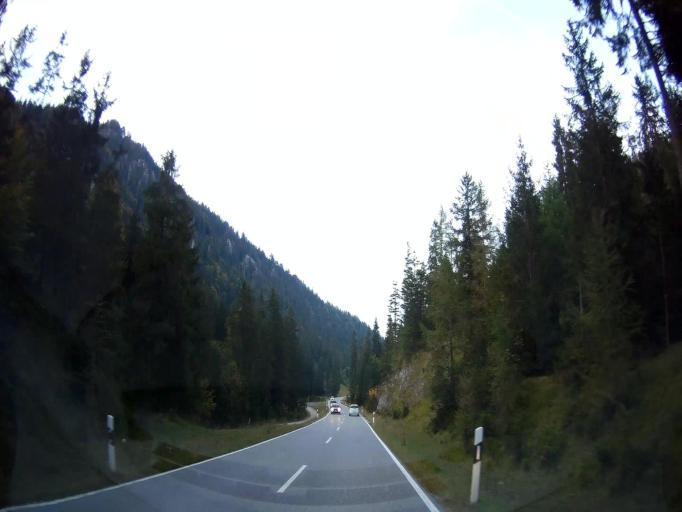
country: DE
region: Bavaria
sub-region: Upper Bavaria
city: Ramsau
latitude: 47.6313
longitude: 12.9093
